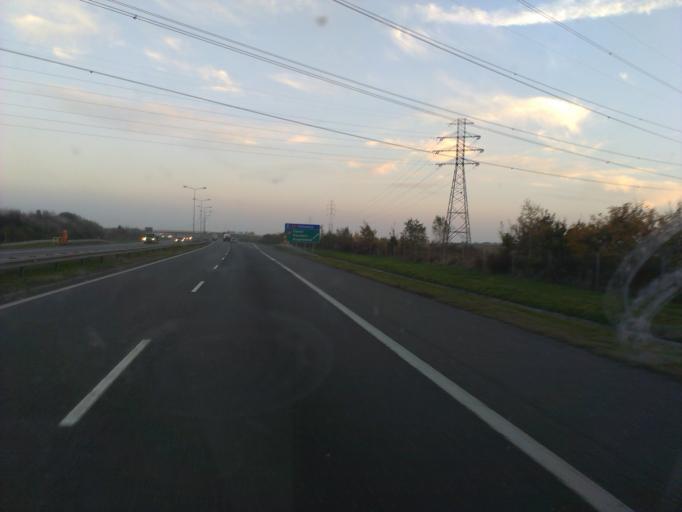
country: PL
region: Opole Voivodeship
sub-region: Powiat opolski
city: Proszkow
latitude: 50.5333
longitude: 17.9084
